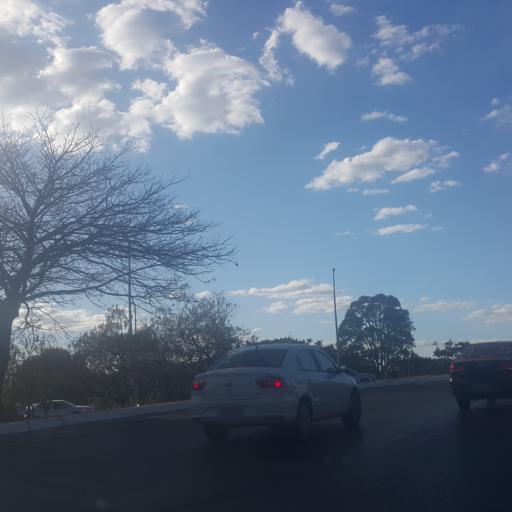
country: BR
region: Federal District
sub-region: Brasilia
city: Brasilia
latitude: -15.8325
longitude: -48.0511
